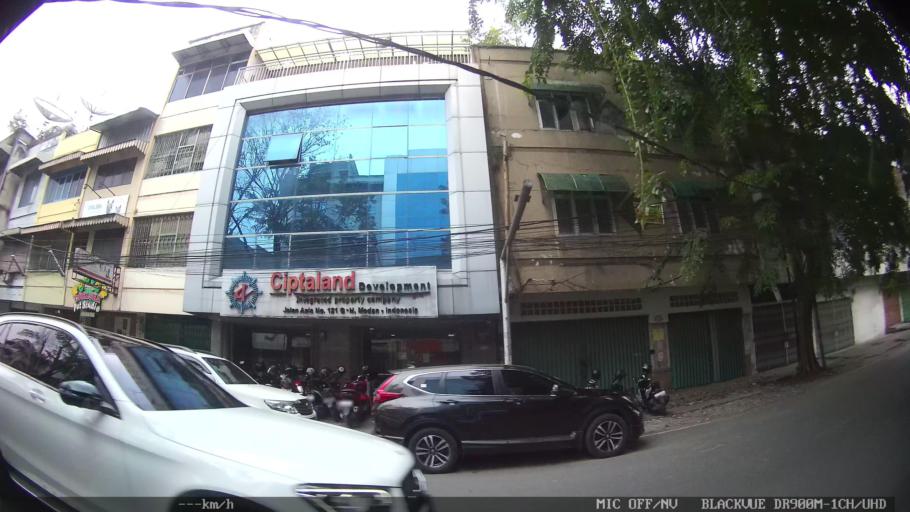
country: ID
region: North Sumatra
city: Medan
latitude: 3.5862
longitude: 98.6974
